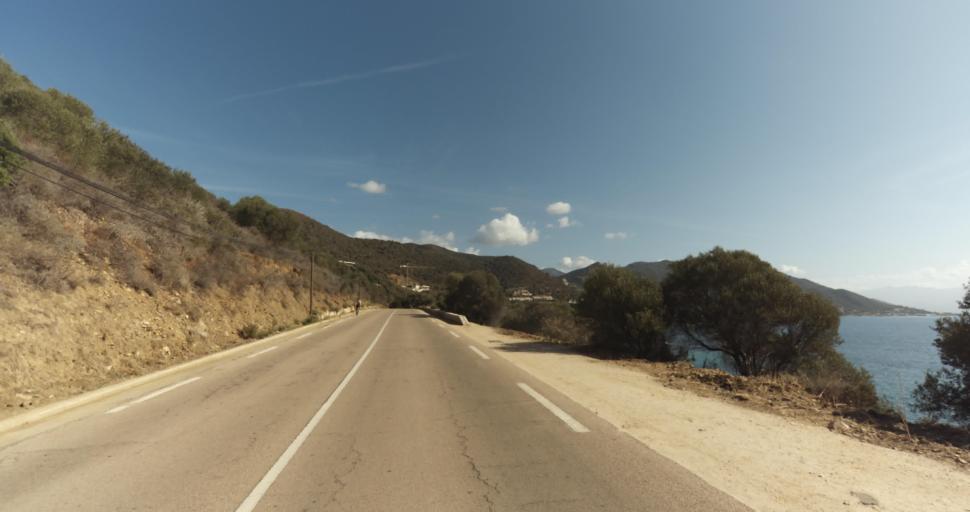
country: FR
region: Corsica
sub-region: Departement de la Corse-du-Sud
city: Ajaccio
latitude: 41.9032
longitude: 8.6260
